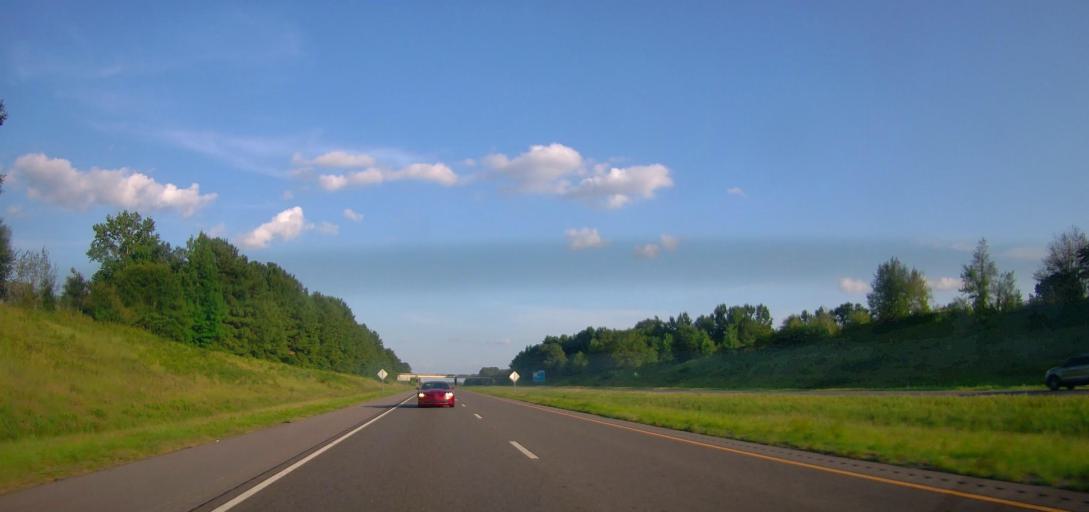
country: US
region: Alabama
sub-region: Walker County
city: Carbon Hill
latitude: 33.8832
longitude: -87.4485
